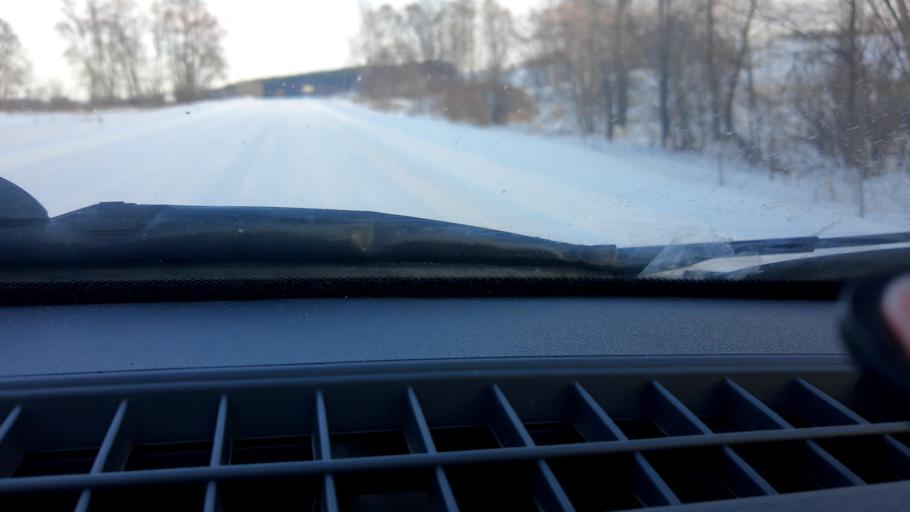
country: RU
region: Bashkortostan
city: Kushnarenkovo
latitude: 55.1405
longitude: 55.6314
